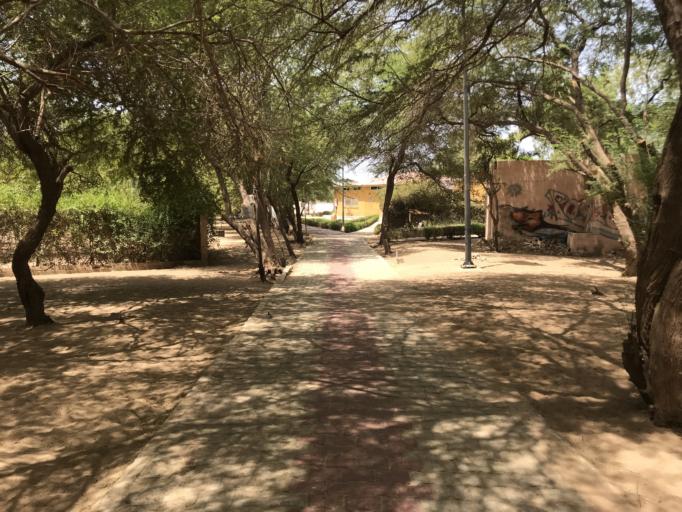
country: SN
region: Saint-Louis
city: Saint-Louis
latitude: 16.0651
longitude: -16.4249
